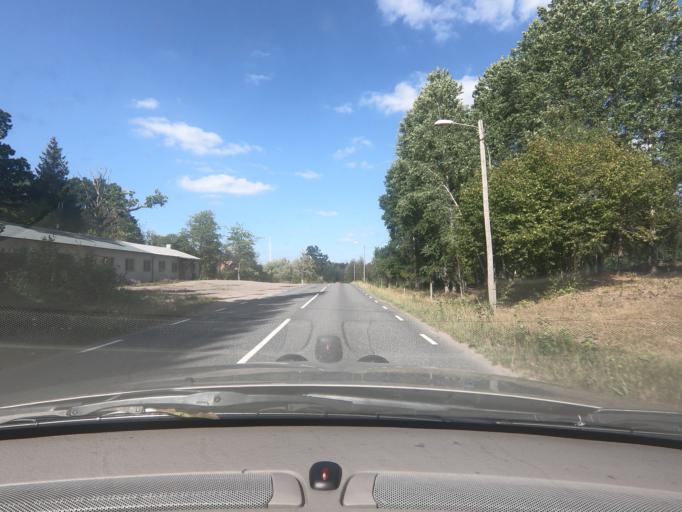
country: SE
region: Joenkoeping
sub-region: Vetlanda Kommun
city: Landsbro
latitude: 57.3260
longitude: 14.8683
